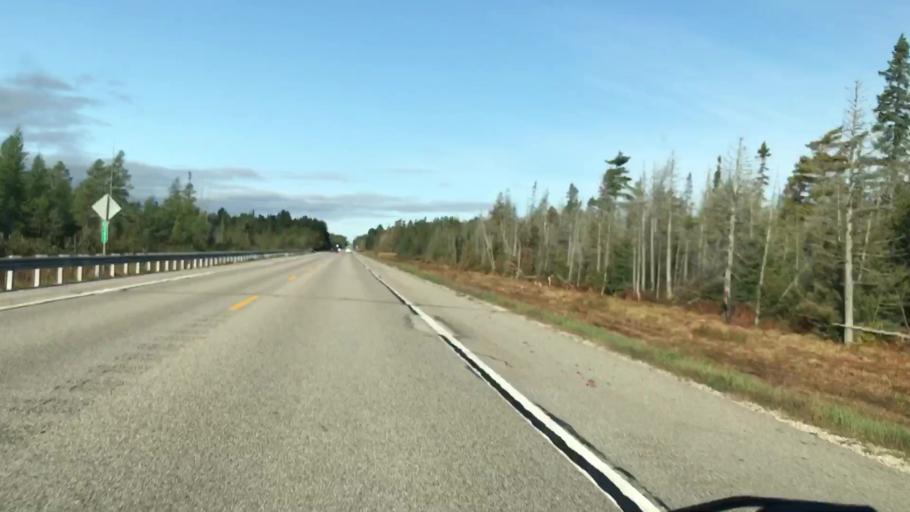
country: US
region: Michigan
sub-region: Luce County
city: Newberry
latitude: 46.3036
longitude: -85.3250
